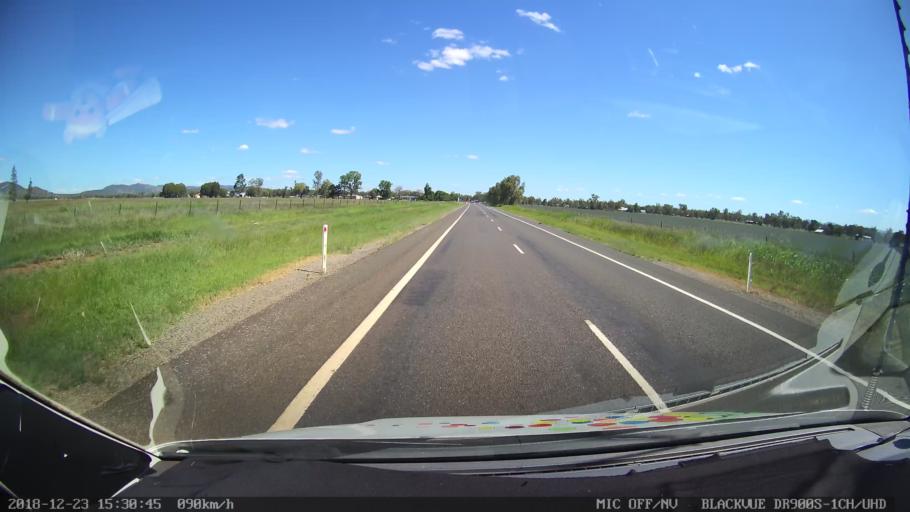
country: AU
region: New South Wales
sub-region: Tamworth Municipality
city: East Tamworth
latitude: -30.9630
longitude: 150.8663
